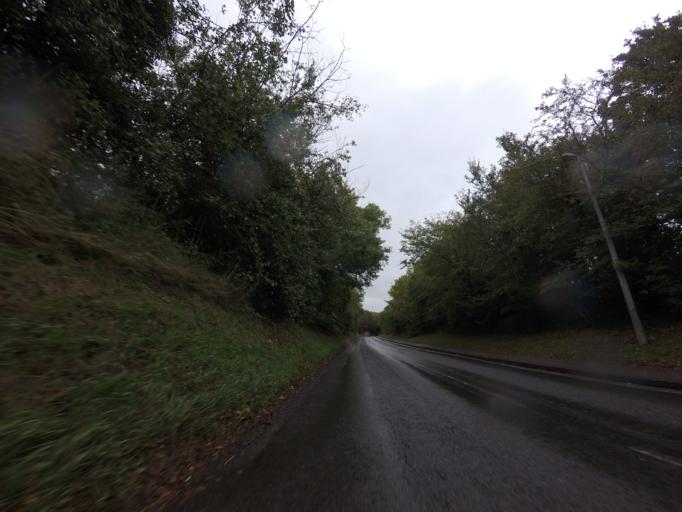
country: GB
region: England
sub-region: Cambridgeshire
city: Wimpole
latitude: 52.1947
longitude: -0.0624
